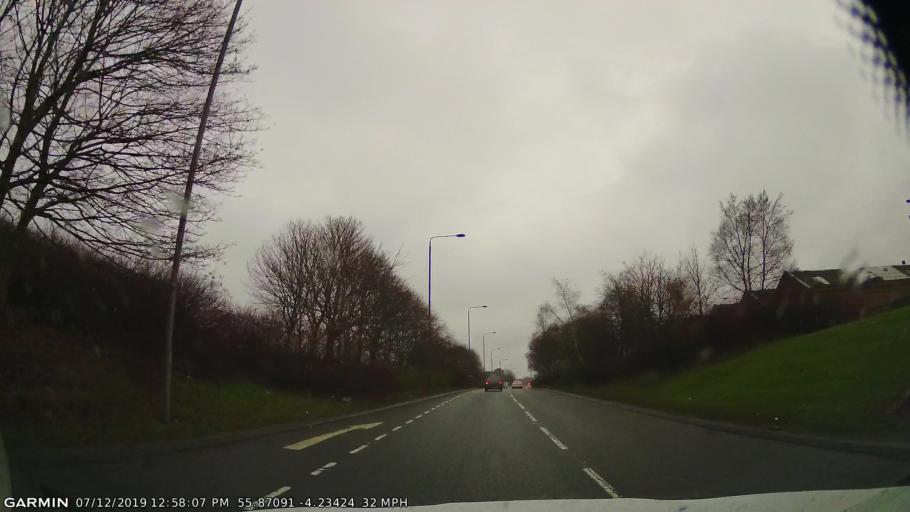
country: GB
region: Scotland
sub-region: Glasgow City
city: Glasgow
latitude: 55.8710
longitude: -4.2342
